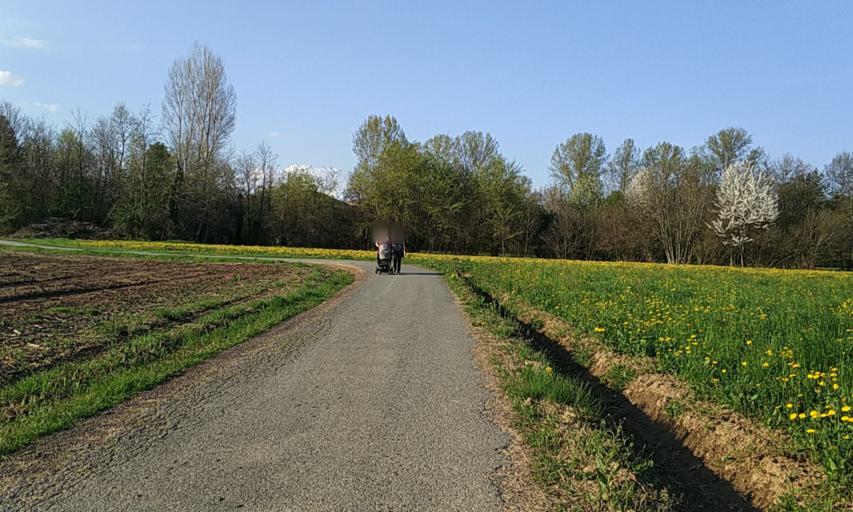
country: IT
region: Piedmont
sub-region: Provincia di Torino
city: San Carlo Canavese
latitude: 45.2451
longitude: 7.5921
